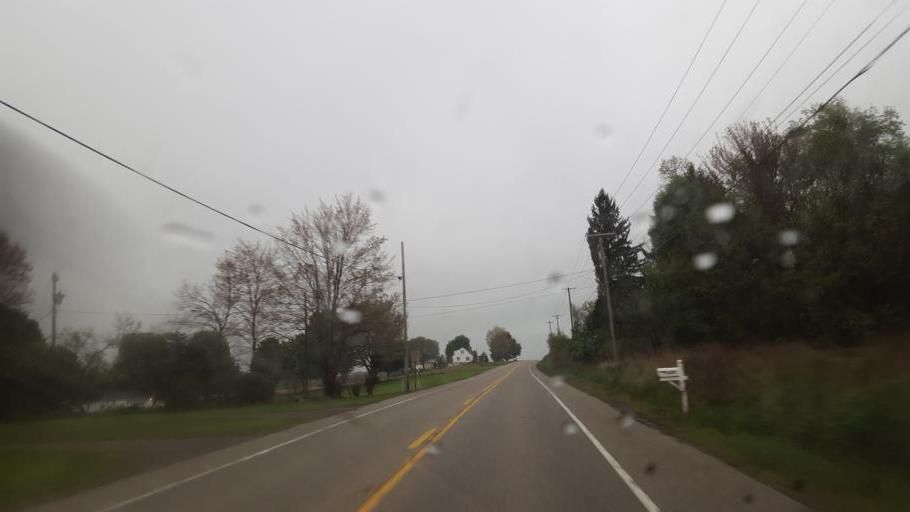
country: US
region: Pennsylvania
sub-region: Mercer County
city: Mercer
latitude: 41.2128
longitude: -80.2398
